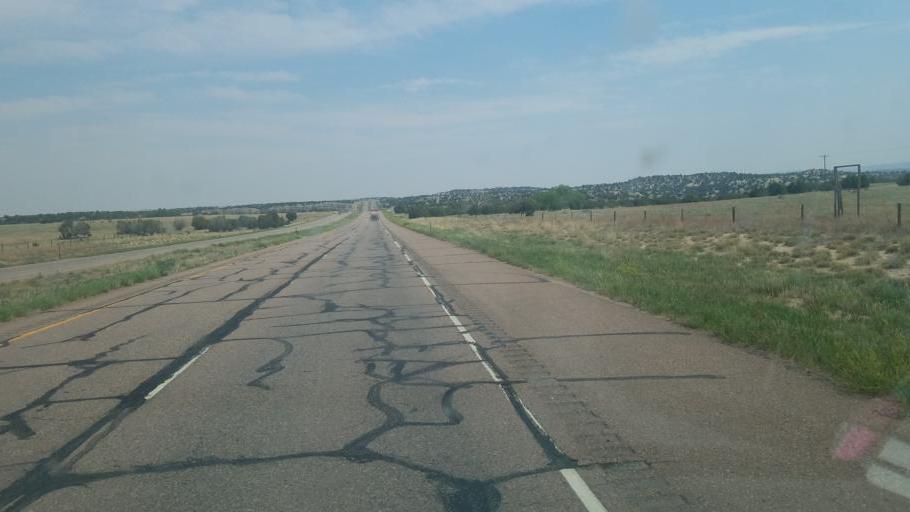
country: US
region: Colorado
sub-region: Fremont County
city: Penrose
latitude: 38.3849
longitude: -104.9595
